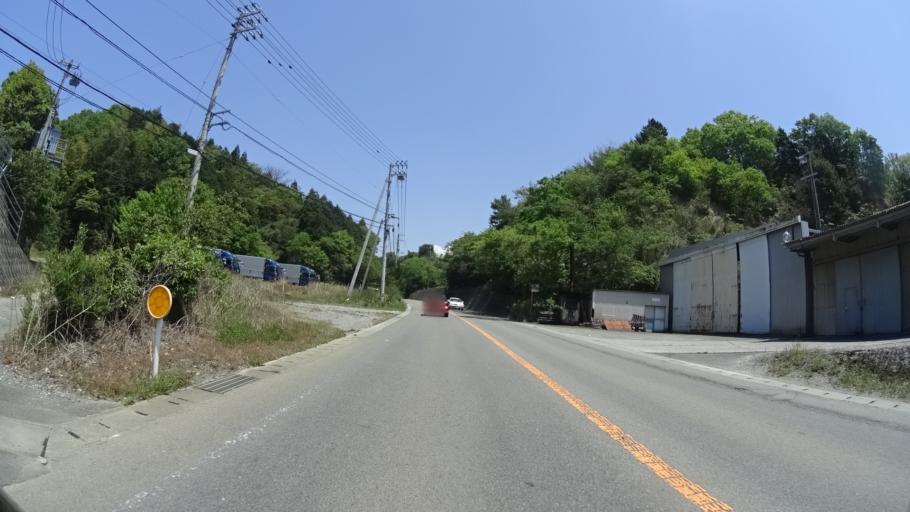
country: JP
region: Ehime
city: Iyo
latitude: 33.7124
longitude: 132.6722
